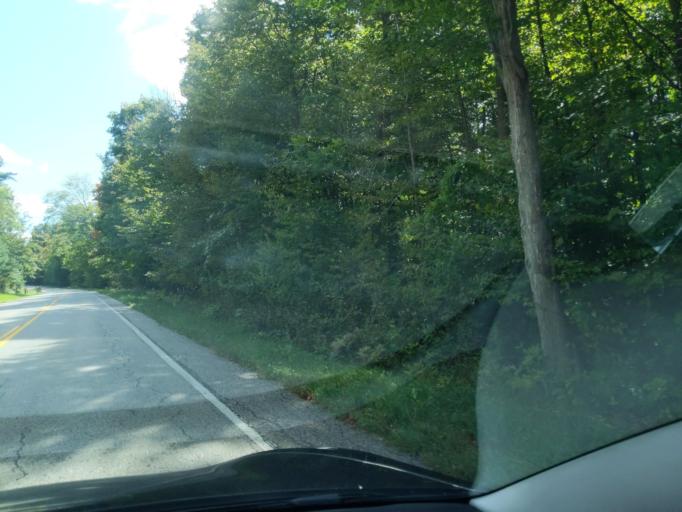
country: US
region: Michigan
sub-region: Antrim County
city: Bellaire
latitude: 45.0770
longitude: -85.3201
